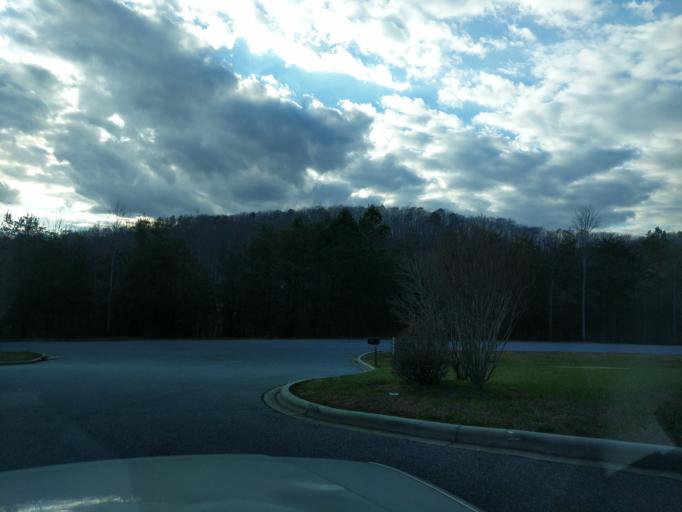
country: US
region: North Carolina
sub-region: McDowell County
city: West Marion
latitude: 35.6458
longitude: -81.9899
